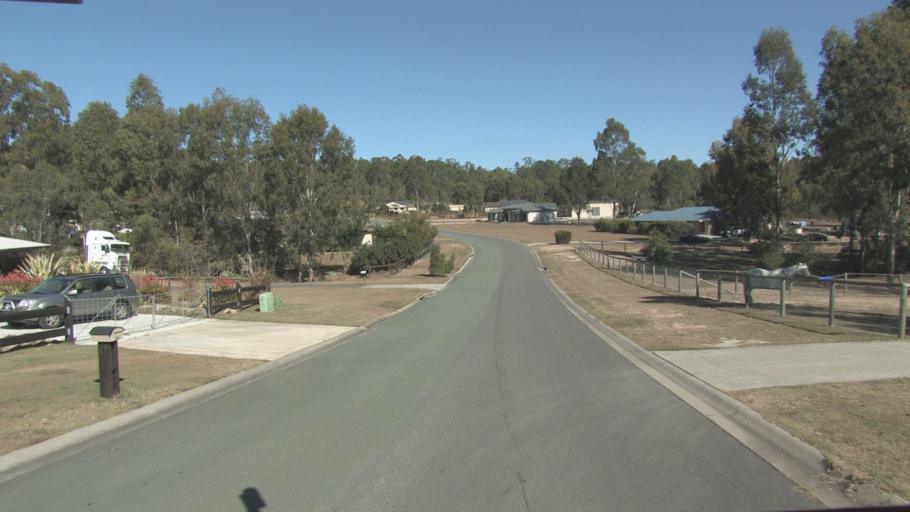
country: AU
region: Queensland
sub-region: Logan
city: Cedar Vale
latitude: -27.8653
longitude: 153.0323
